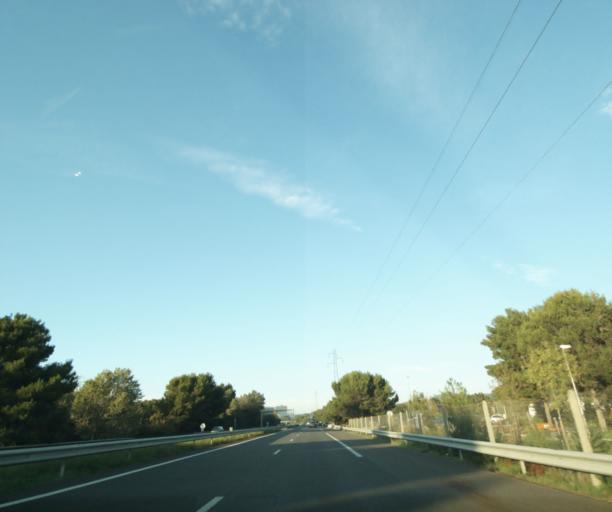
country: FR
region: Provence-Alpes-Cote d'Azur
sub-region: Departement des Bouches-du-Rhone
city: Aubagne
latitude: 43.2998
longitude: 5.5903
